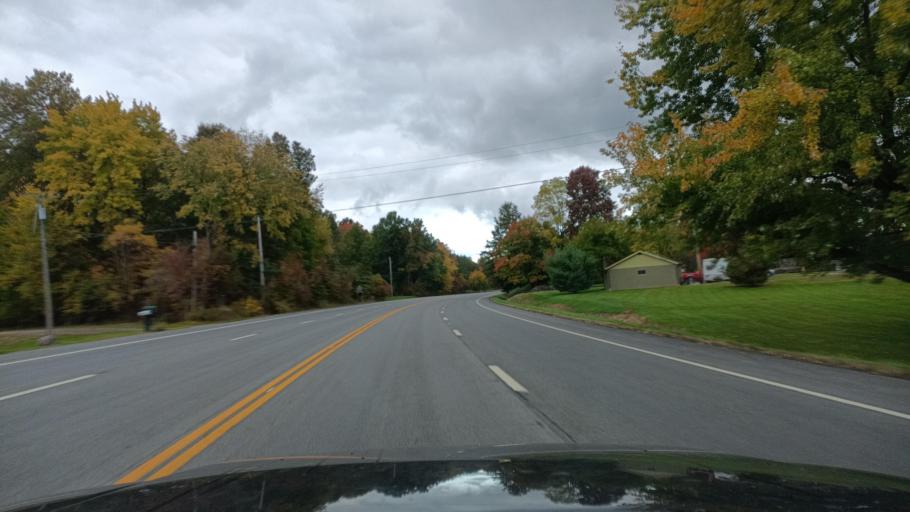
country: US
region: Ohio
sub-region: Trumbull County
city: Warren
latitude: 41.2054
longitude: -80.8442
